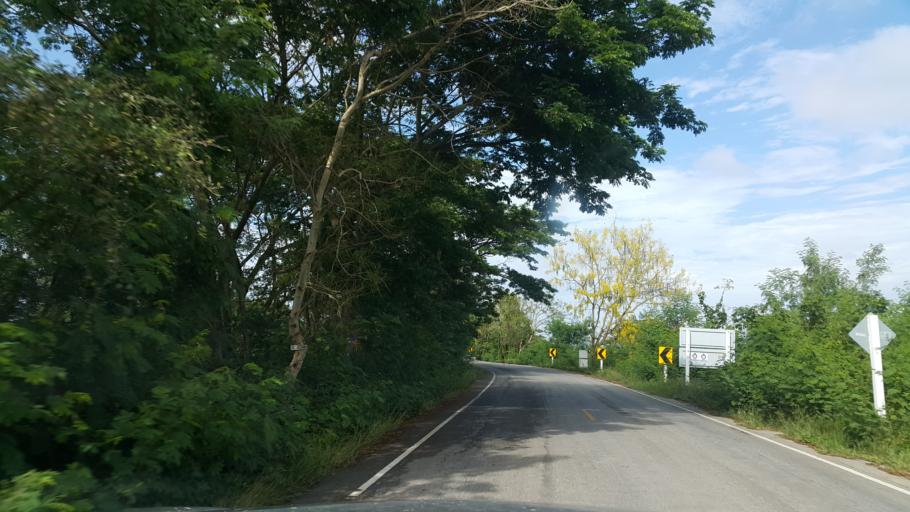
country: TH
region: Chiang Rai
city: Wiang Chai
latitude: 19.9409
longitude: 99.9188
